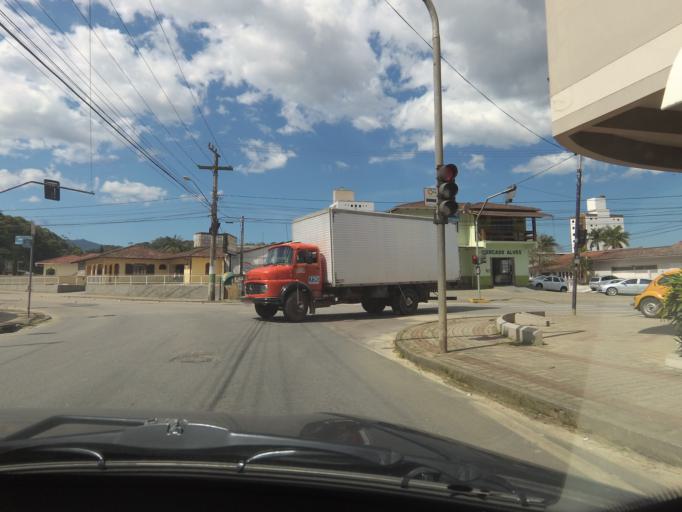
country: BR
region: Santa Catarina
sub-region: Brusque
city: Brusque
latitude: -27.0814
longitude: -48.9180
